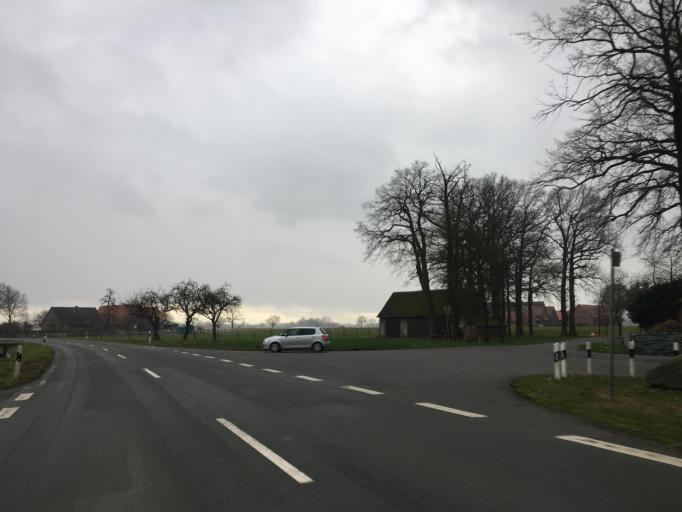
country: DE
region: North Rhine-Westphalia
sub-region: Regierungsbezirk Munster
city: Senden
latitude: 51.8560
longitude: 7.4287
